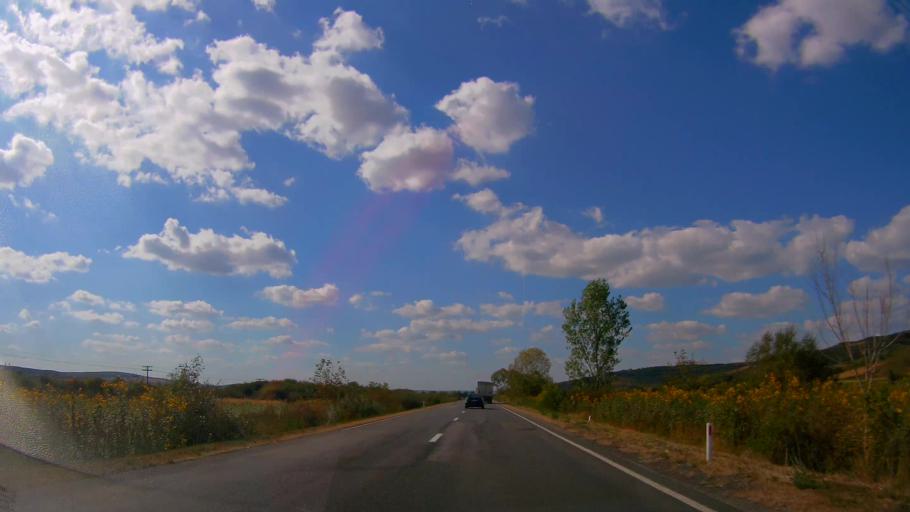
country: RO
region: Salaj
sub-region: Comuna Bocsa
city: Bocsa
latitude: 47.3216
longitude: 22.8909
